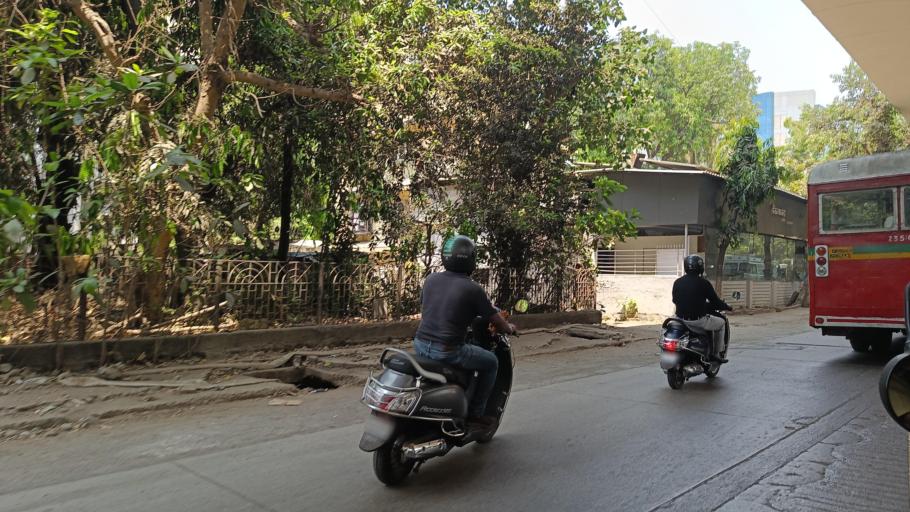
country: IN
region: Maharashtra
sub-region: Mumbai Suburban
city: Mumbai
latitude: 19.0724
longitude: 72.8642
